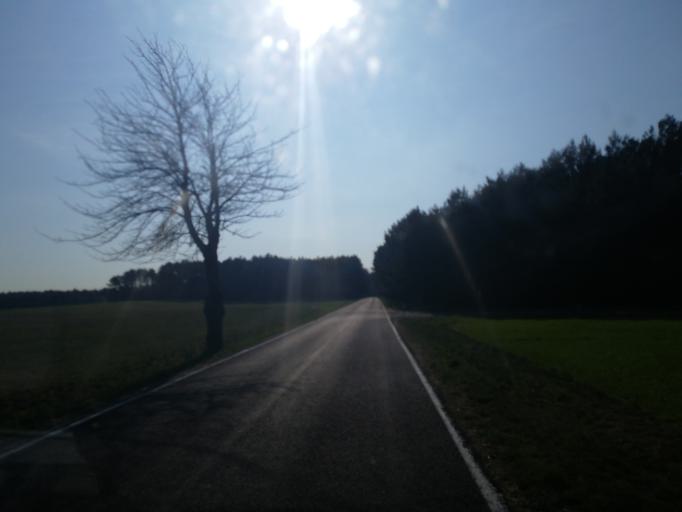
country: DE
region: Brandenburg
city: Sonnewalde
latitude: 51.7753
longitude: 13.6362
